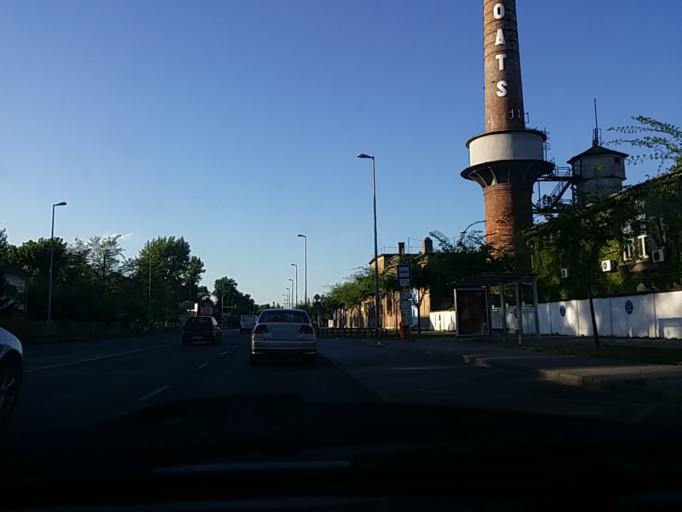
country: HU
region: Budapest
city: Budapest IV. keruelet
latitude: 47.5835
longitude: 19.0819
